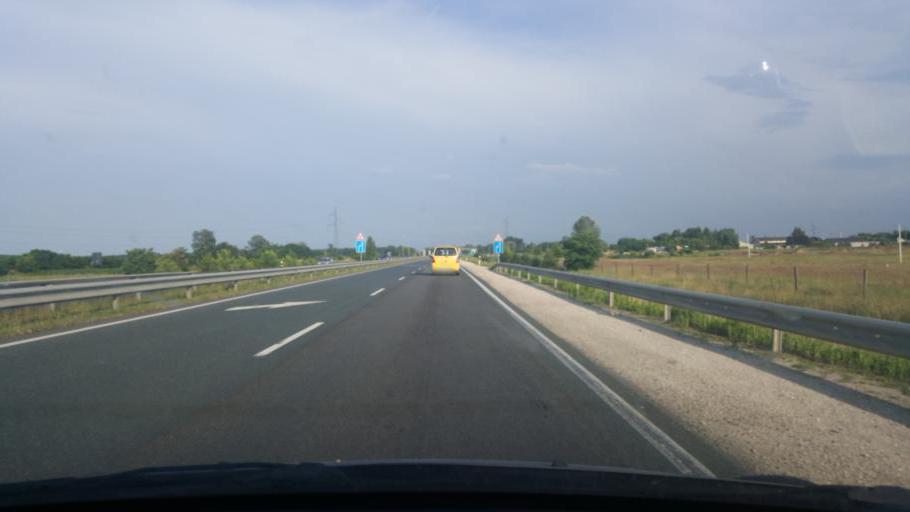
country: HU
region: Pest
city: Ullo
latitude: 47.3974
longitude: 19.3613
